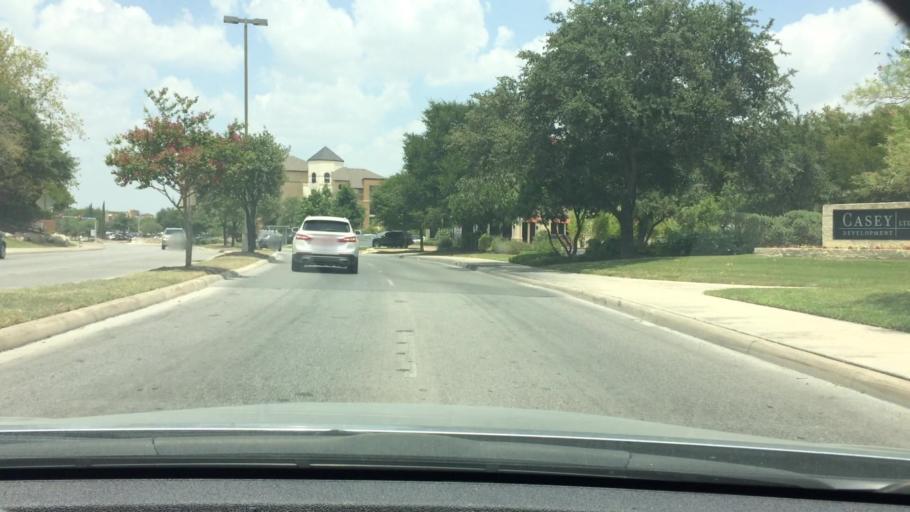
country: US
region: Texas
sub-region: Bexar County
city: Olmos Park
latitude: 29.4924
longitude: -98.4800
